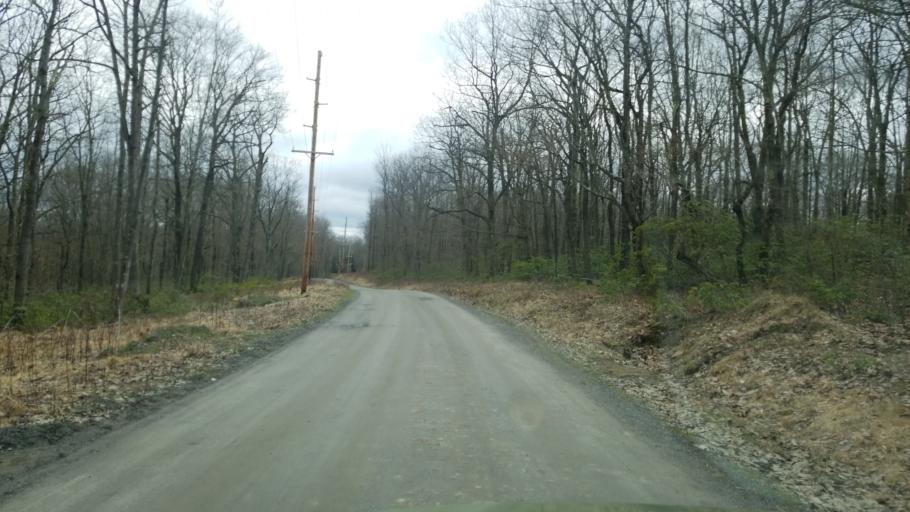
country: US
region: Pennsylvania
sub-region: Clearfield County
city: Shiloh
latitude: 41.1715
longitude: -78.2937
